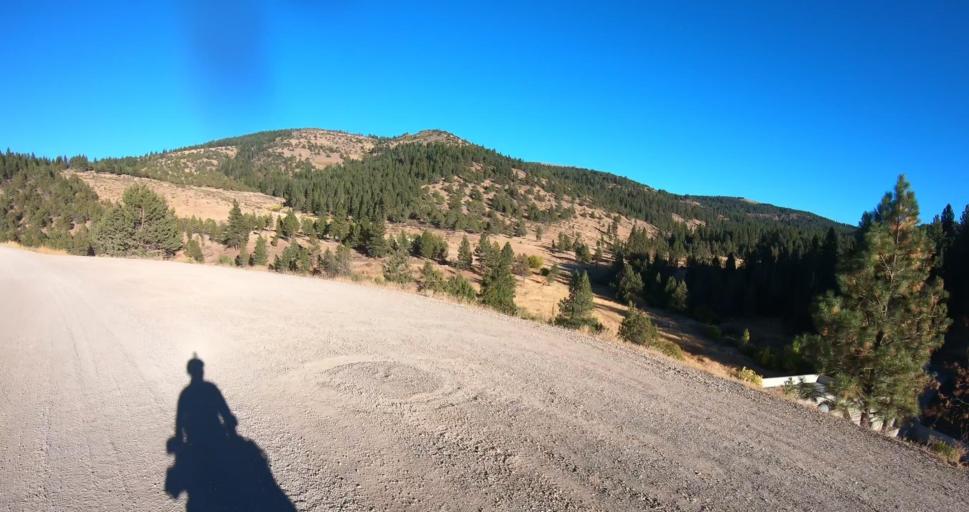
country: US
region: Oregon
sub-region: Lake County
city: Lakeview
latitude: 42.1929
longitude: -120.3091
